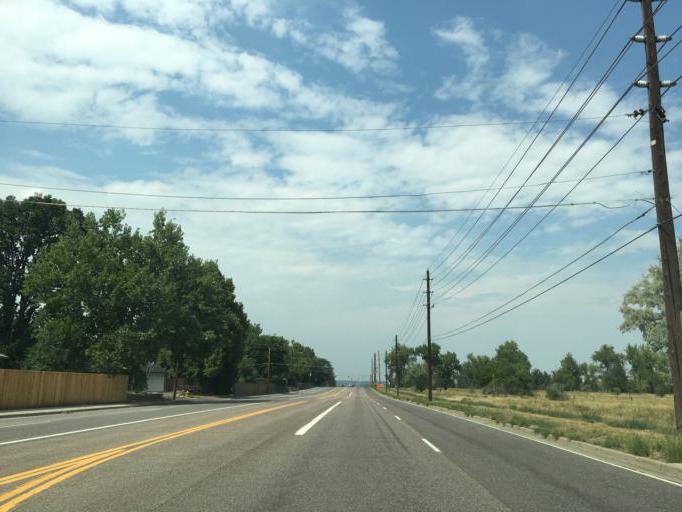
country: US
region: Colorado
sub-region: Jefferson County
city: Wheat Ridge
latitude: 39.7584
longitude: -105.1095
